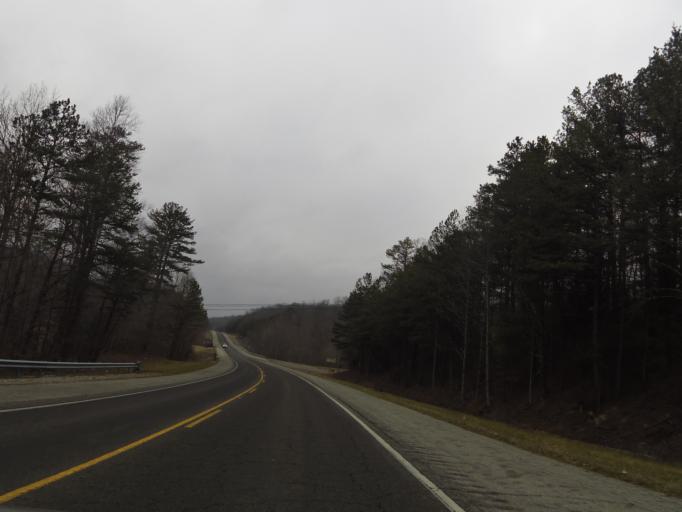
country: US
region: Tennessee
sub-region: Morgan County
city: Wartburg
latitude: 36.1267
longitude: -84.6140
